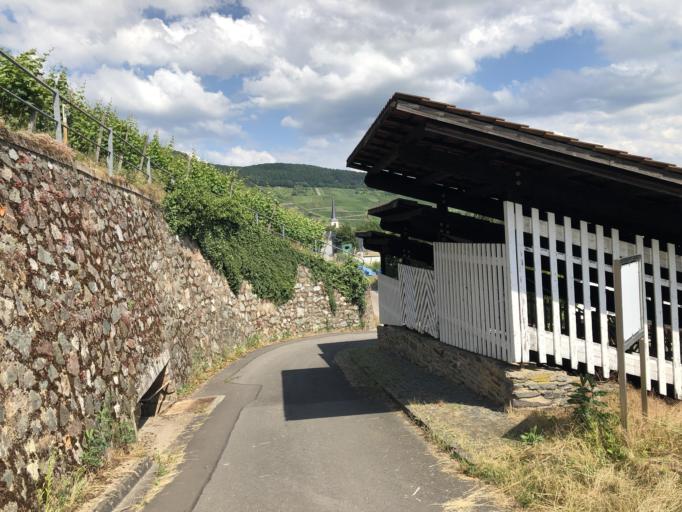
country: DE
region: Rheinland-Pfalz
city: Piesport
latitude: 49.8859
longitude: 6.9113
